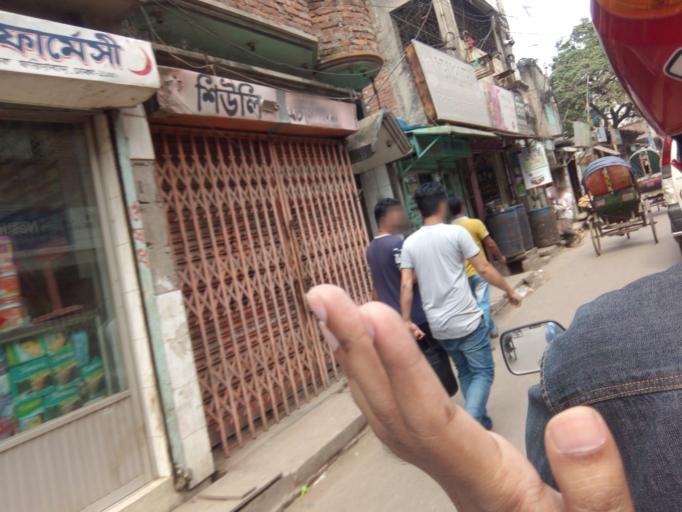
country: BD
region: Dhaka
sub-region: Dhaka
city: Dhaka
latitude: 23.6993
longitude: 90.4217
